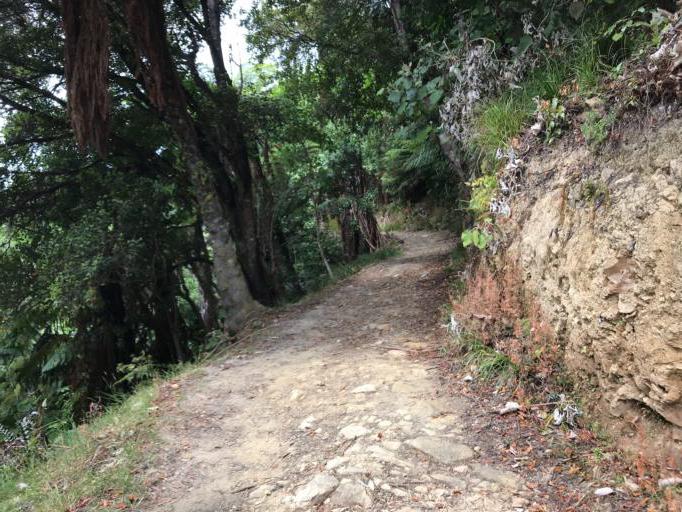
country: NZ
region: Marlborough
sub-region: Marlborough District
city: Picton
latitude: -41.1162
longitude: 174.2042
